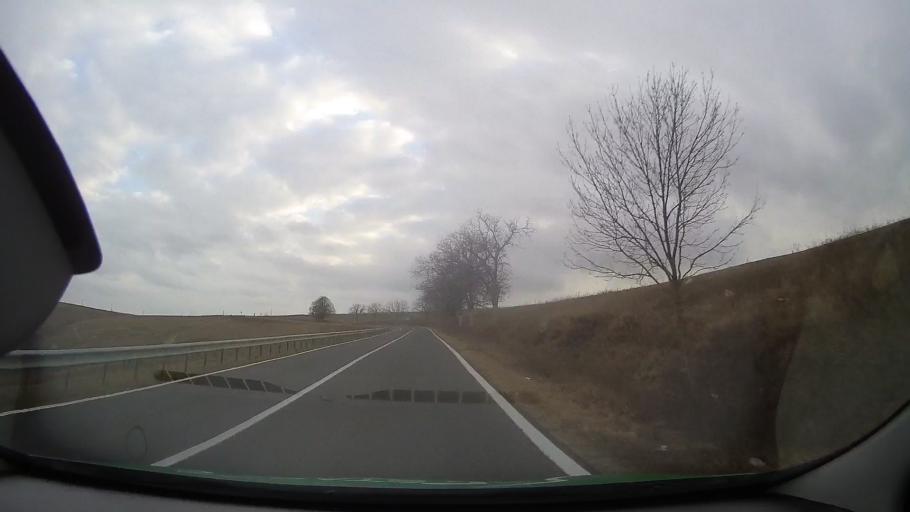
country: RO
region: Constanta
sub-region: Comuna Deleni
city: Deleni
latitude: 44.0967
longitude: 28.0169
